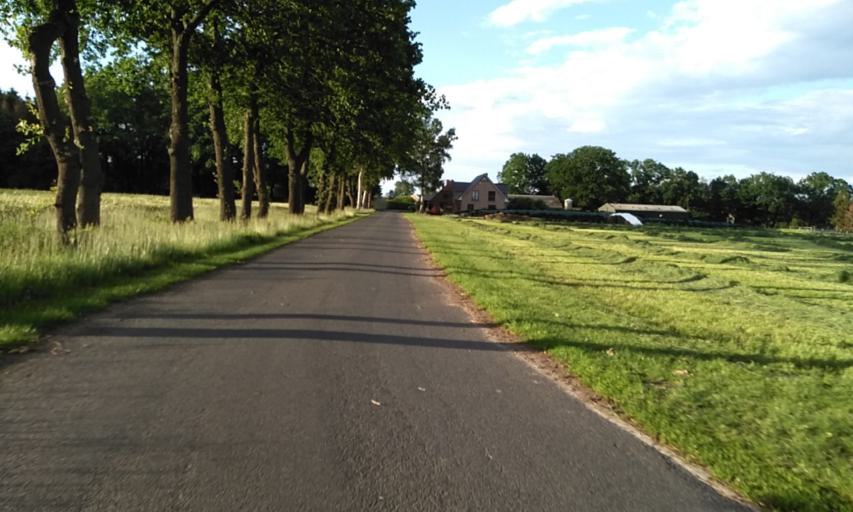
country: DE
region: Lower Saxony
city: Anderlingen
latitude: 53.3850
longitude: 9.3119
